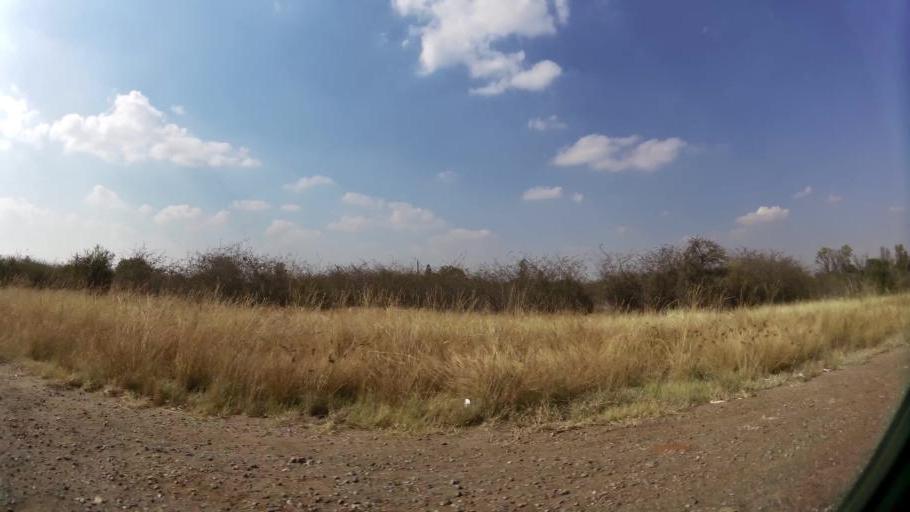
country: ZA
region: North-West
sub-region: Bojanala Platinum District Municipality
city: Rustenburg
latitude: -25.5155
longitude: 27.1009
